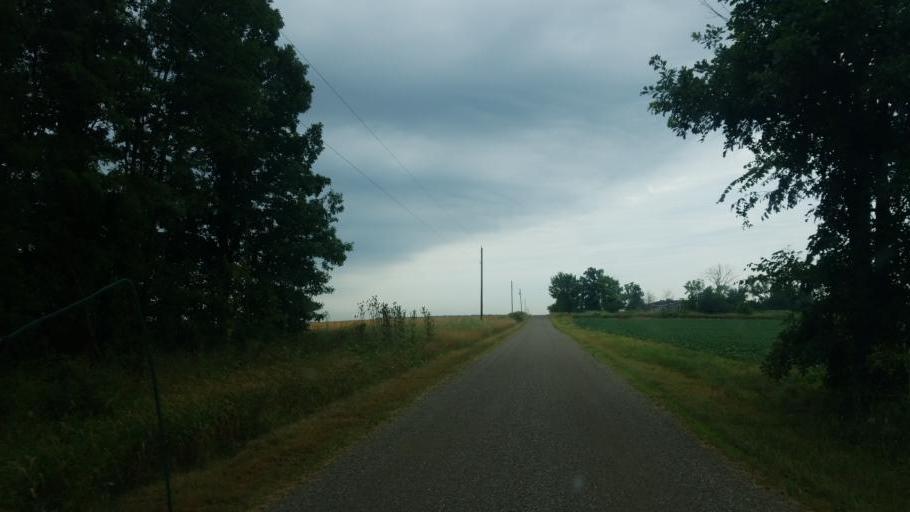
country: US
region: Indiana
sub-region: Steuben County
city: Hamilton
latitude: 41.4780
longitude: -84.9105
